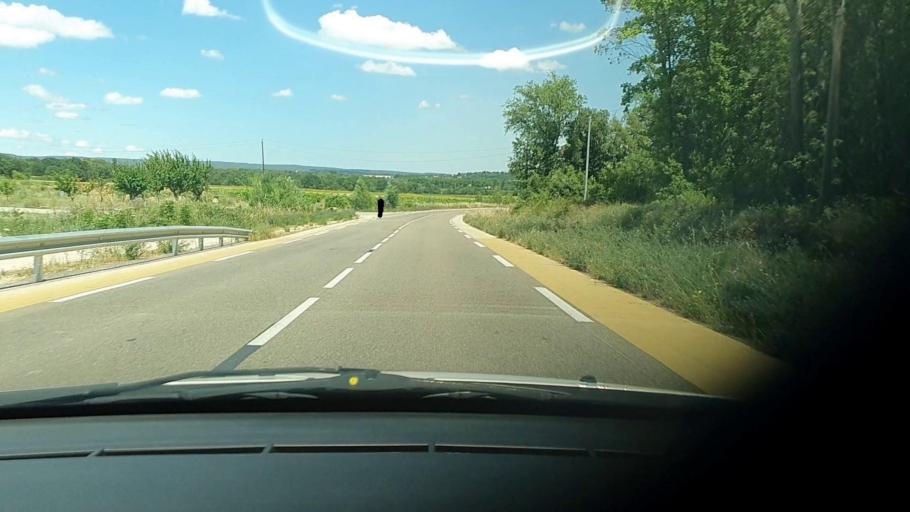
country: FR
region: Languedoc-Roussillon
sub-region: Departement du Gard
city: Blauzac
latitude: 43.9894
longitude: 4.3848
